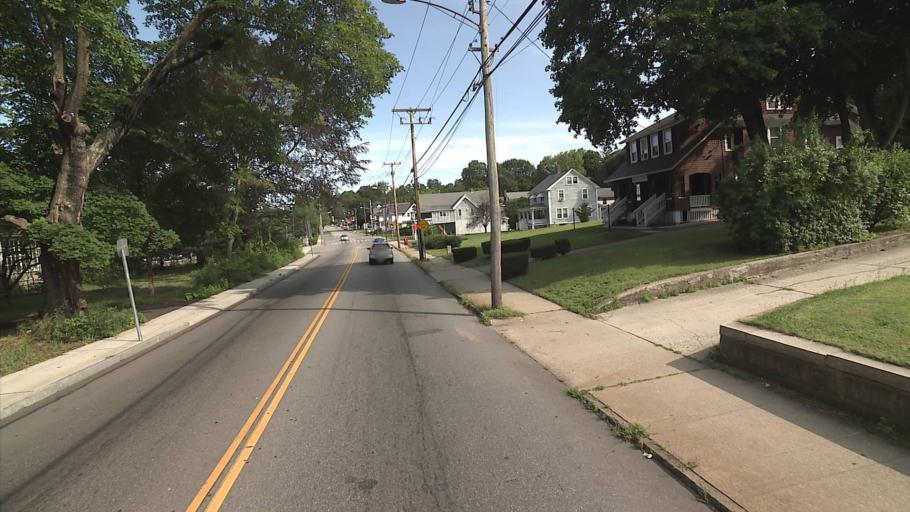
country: US
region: Connecticut
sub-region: New London County
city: Norwich
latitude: 41.5418
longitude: -72.0859
